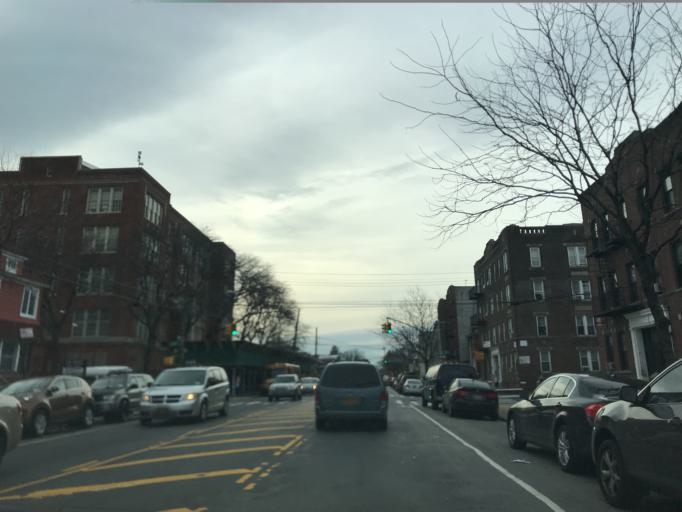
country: US
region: New York
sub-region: Kings County
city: Brooklyn
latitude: 40.6538
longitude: -73.9319
